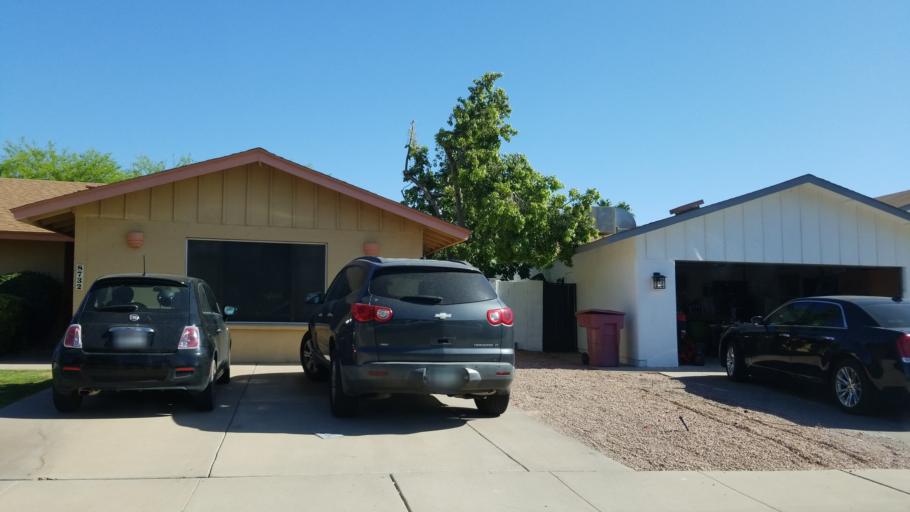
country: US
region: Arizona
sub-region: Maricopa County
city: Scottsdale
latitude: 33.4920
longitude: -111.8930
